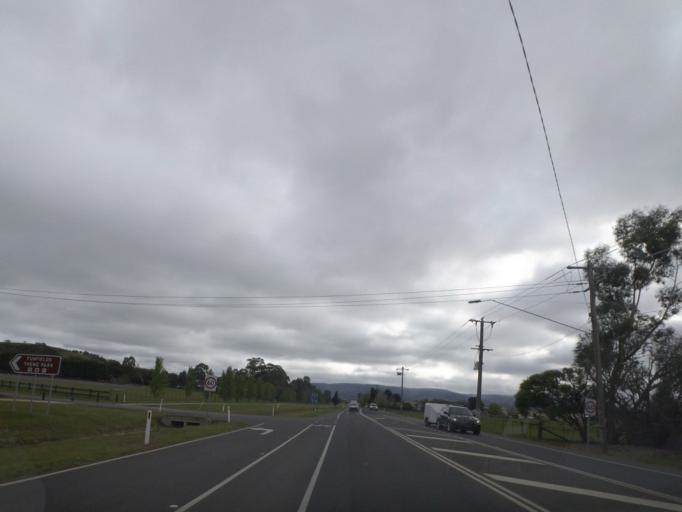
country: AU
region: Victoria
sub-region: Whittlesea
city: Whittlesea
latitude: -37.5214
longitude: 145.1132
